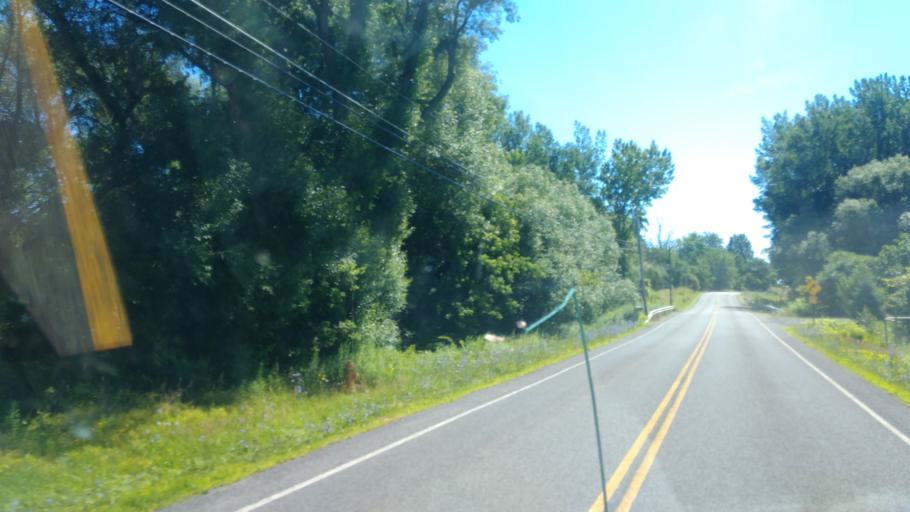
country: US
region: New York
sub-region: Wayne County
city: Williamson
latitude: 43.2835
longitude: -77.1386
